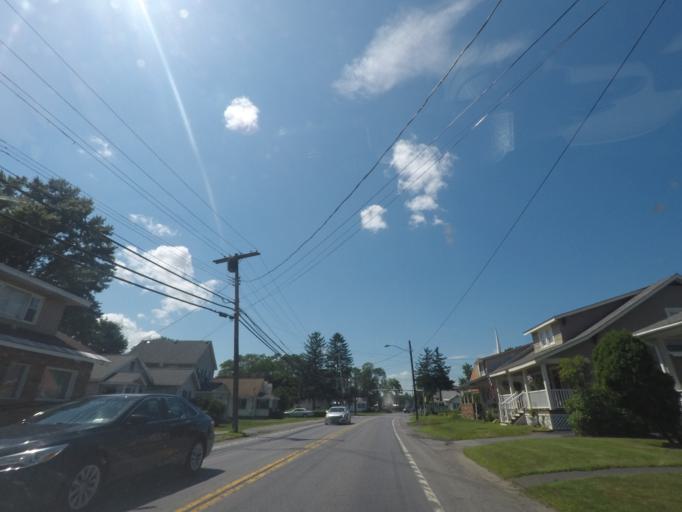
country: US
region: New York
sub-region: Schenectady County
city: Rotterdam
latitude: 42.7885
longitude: -73.9771
